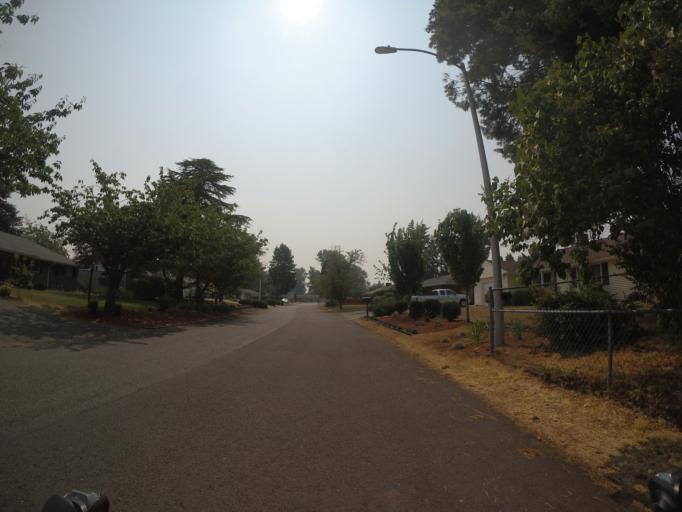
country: US
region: Washington
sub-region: Pierce County
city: Lakewood
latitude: 47.1607
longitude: -122.5094
